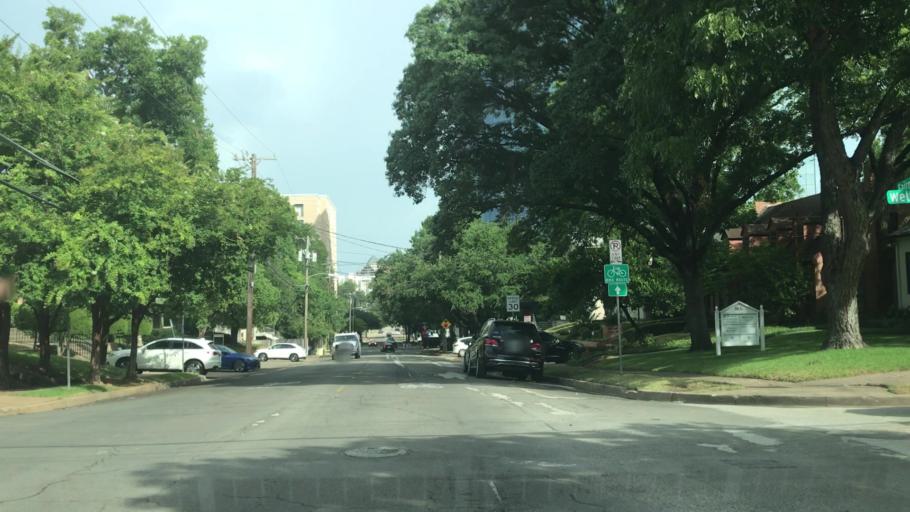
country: US
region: Texas
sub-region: Dallas County
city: Dallas
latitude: 32.8041
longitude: -96.8129
